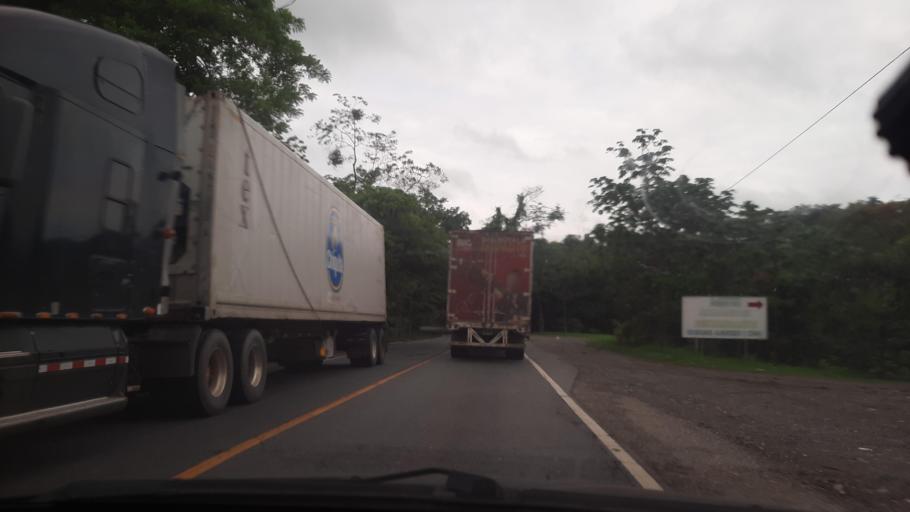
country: GT
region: Izabal
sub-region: Municipio de Los Amates
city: Los Amates
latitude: 15.2774
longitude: -89.0745
